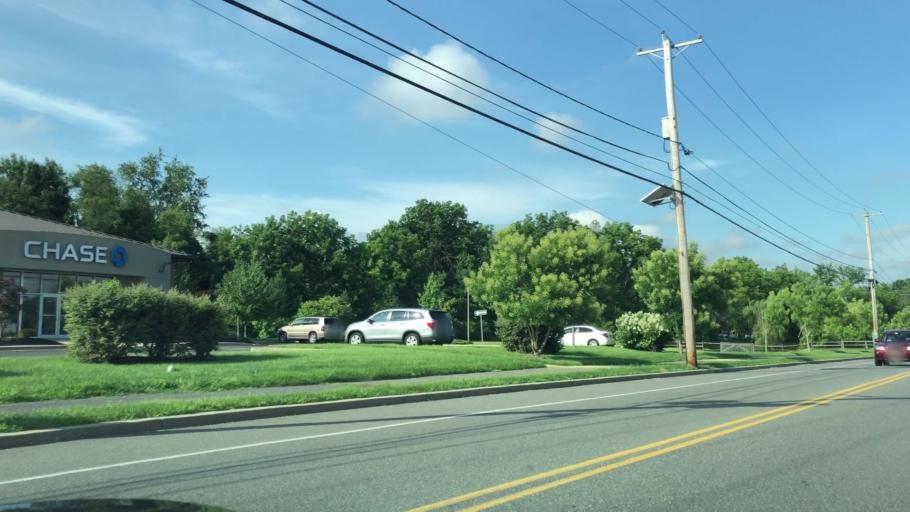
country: US
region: New Jersey
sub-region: Mercer County
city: Pennington
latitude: 40.3002
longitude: -74.7811
